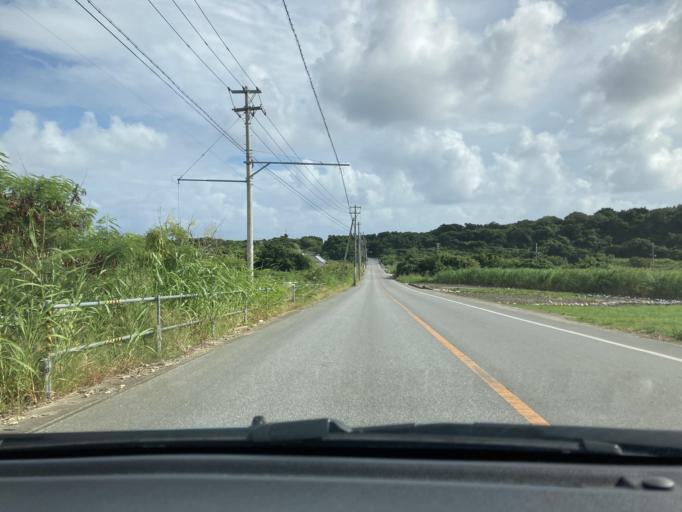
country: JP
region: Okinawa
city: Itoman
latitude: 26.1015
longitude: 127.6972
